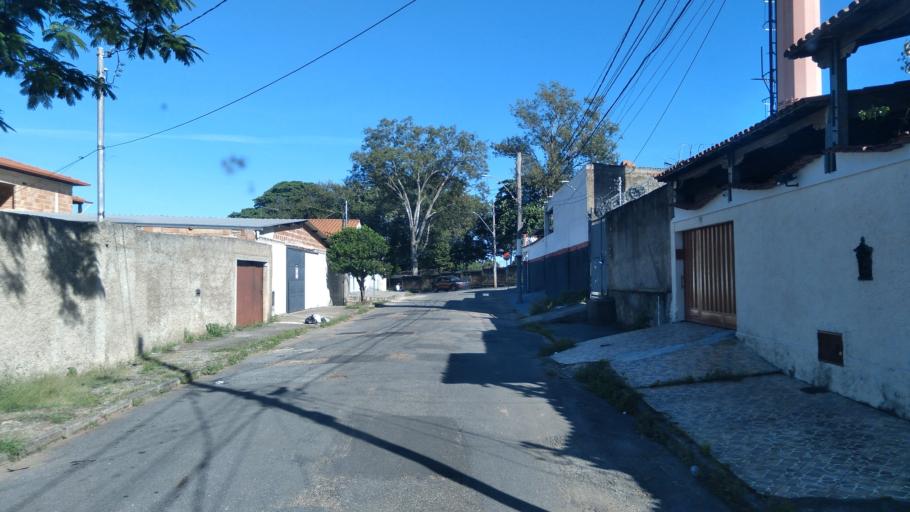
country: BR
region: Minas Gerais
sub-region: Belo Horizonte
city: Belo Horizonte
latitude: -19.9201
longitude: -43.8978
